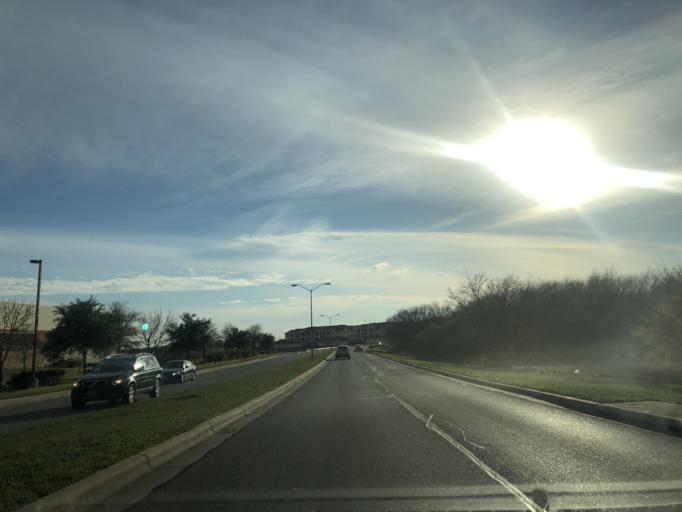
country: US
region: Texas
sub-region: Travis County
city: Windemere
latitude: 30.4362
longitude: -97.6477
